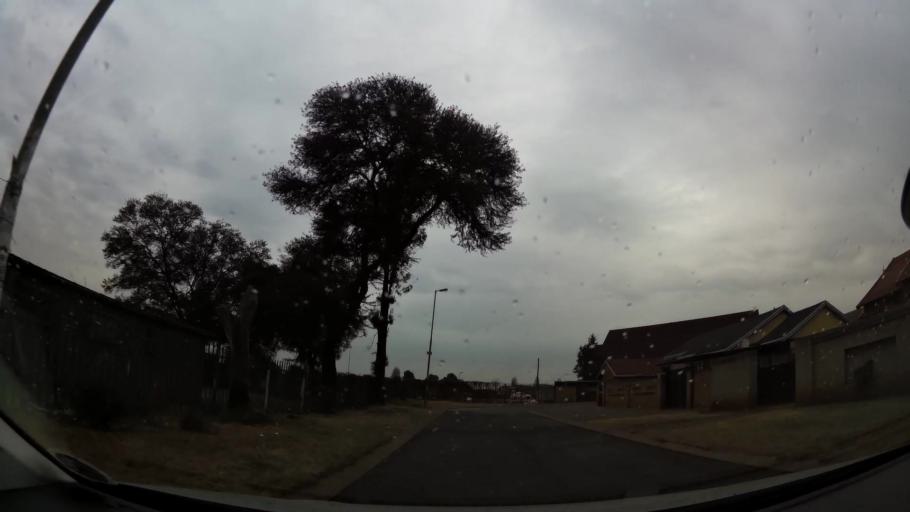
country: ZA
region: Gauteng
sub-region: City of Johannesburg Metropolitan Municipality
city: Soweto
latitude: -26.2456
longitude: 27.8763
